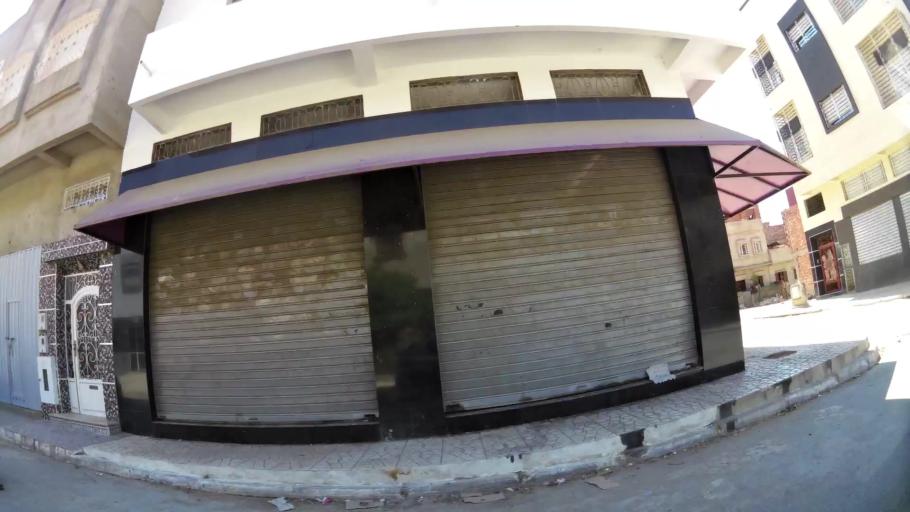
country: MA
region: Gharb-Chrarda-Beni Hssen
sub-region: Kenitra Province
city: Kenitra
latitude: 34.2304
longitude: -6.5515
